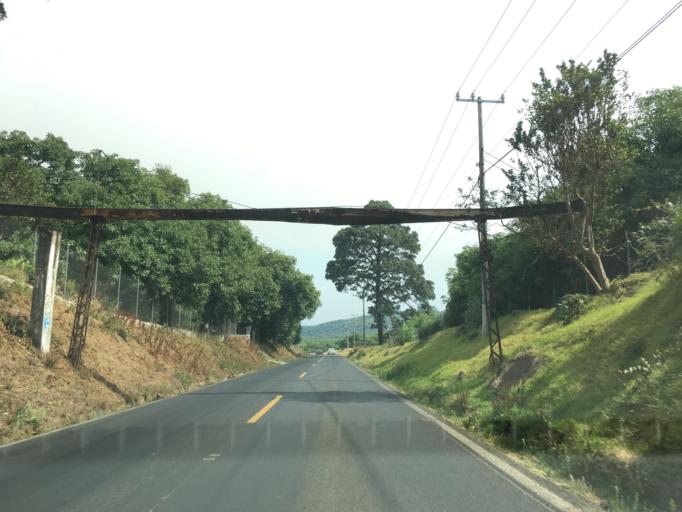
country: MX
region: Michoacan
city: Nuevo San Juan Parangaricutiro
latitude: 19.4020
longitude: -102.1089
